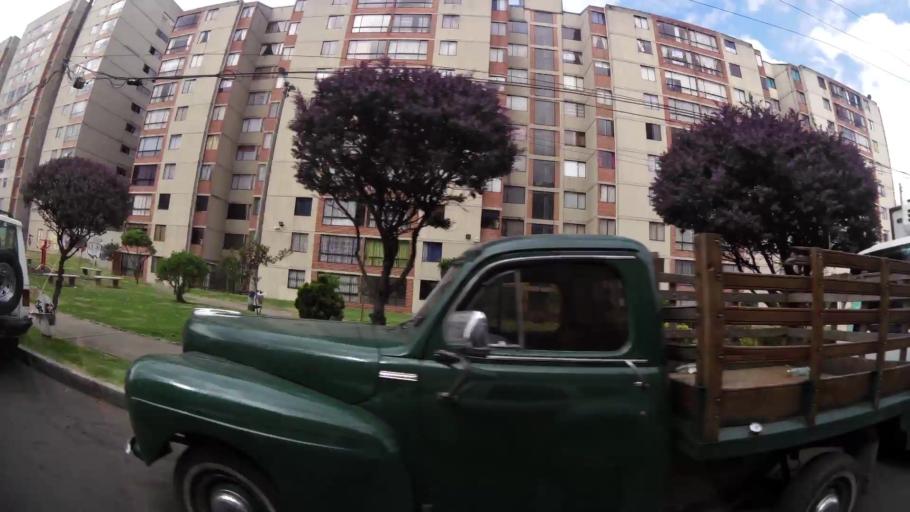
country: CO
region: Bogota D.C.
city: Bogota
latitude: 4.6134
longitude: -74.1089
